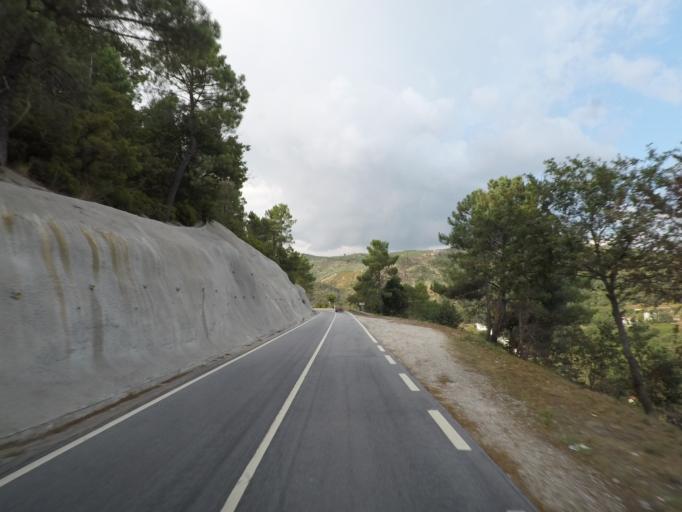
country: PT
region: Porto
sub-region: Baiao
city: Valadares
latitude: 41.2119
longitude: -7.9769
